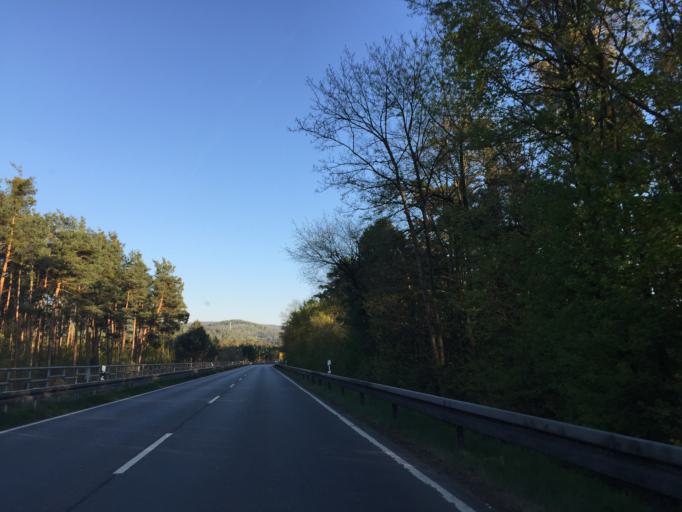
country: DE
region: Hesse
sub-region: Regierungsbezirk Darmstadt
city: Bickenbach
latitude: 49.7716
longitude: 8.6195
